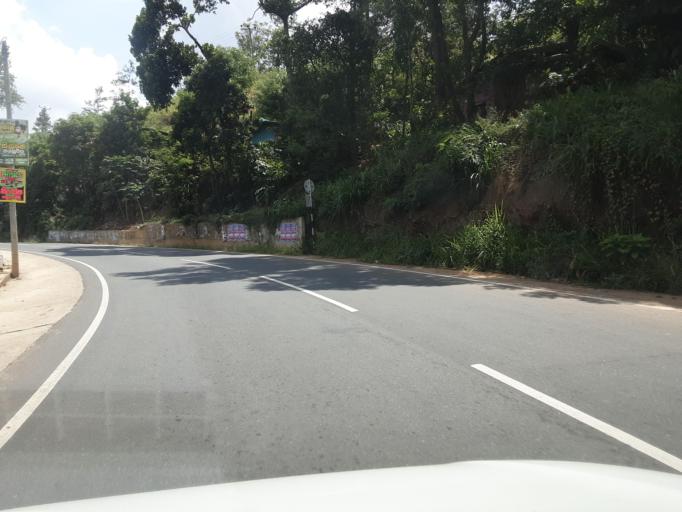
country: LK
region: Central
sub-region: Nuwara Eliya District
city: Nuwara Eliya
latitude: 6.9179
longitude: 80.9039
